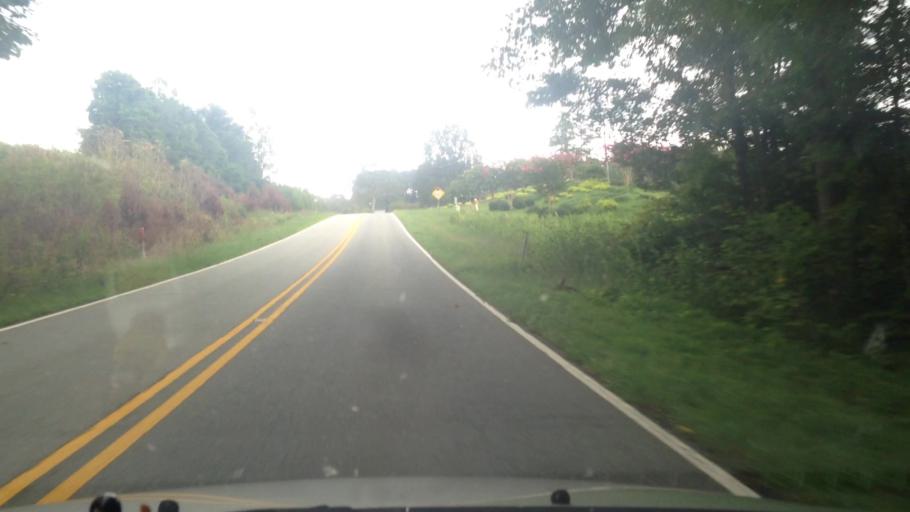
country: US
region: North Carolina
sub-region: Forsyth County
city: Walkertown
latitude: 36.1979
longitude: -80.1652
